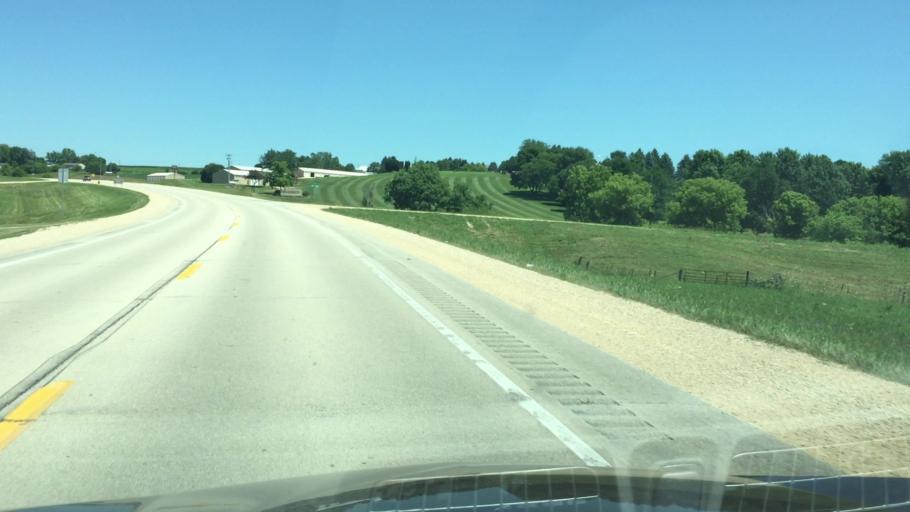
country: US
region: Iowa
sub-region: Jackson County
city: Maquoketa
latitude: 42.0595
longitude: -90.6958
